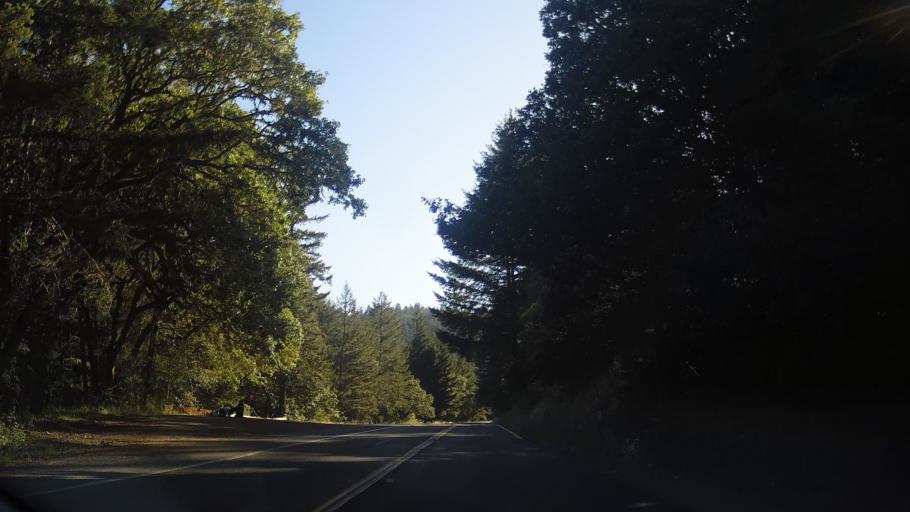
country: US
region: California
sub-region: Mendocino County
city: Brooktrails
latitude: 39.3893
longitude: -123.4216
